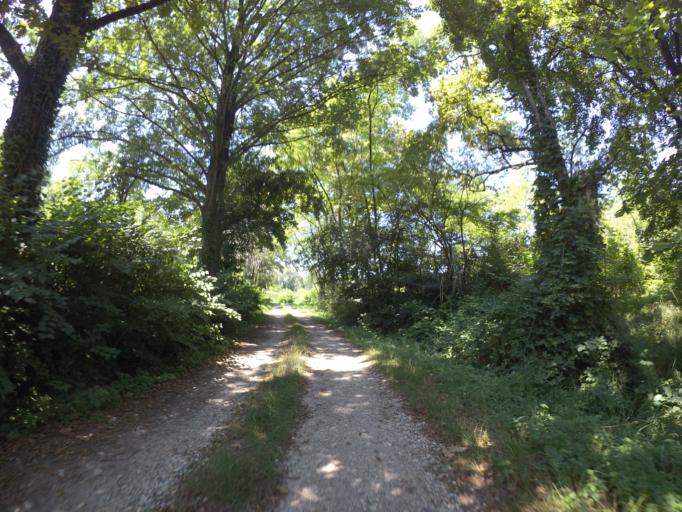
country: IT
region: Friuli Venezia Giulia
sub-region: Provincia di Udine
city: Bertiolo
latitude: 45.9279
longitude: 13.0791
